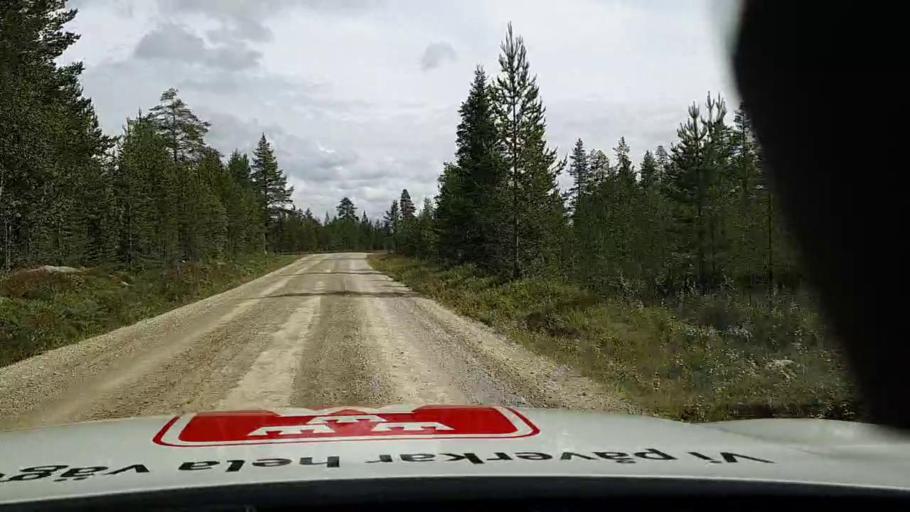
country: SE
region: Jaemtland
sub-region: Are Kommun
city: Jarpen
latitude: 62.5339
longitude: 13.4805
